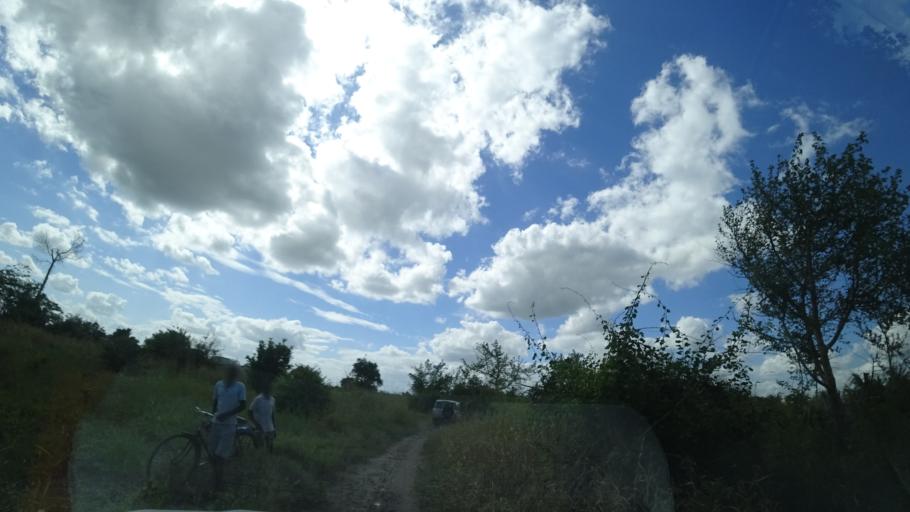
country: MZ
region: Sofala
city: Dondo
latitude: -19.3376
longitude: 34.5823
